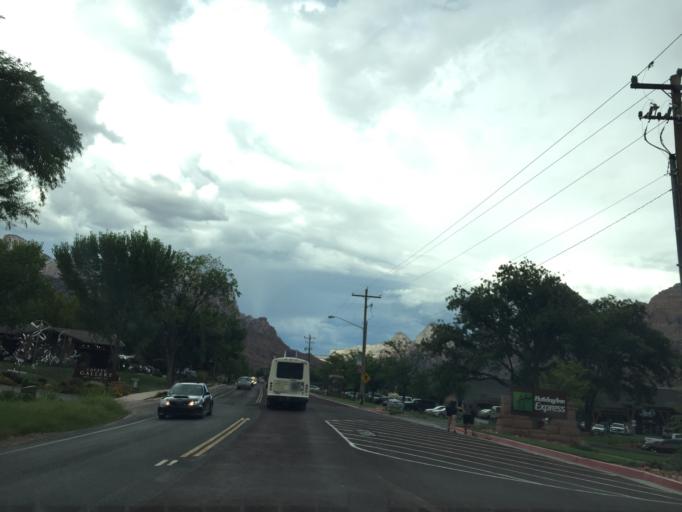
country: US
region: Utah
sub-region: Washington County
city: Hildale
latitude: 37.1831
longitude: -113.0037
